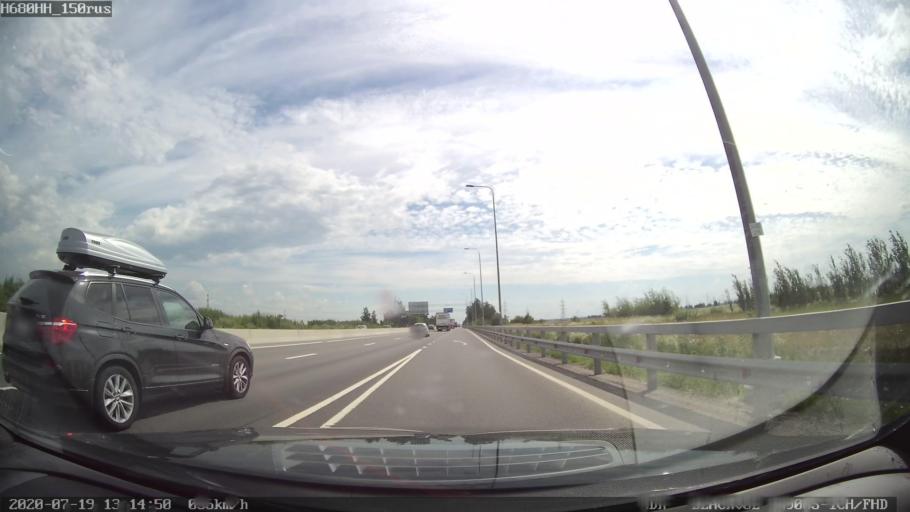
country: RU
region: St.-Petersburg
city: Kolpino
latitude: 59.7300
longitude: 30.5310
